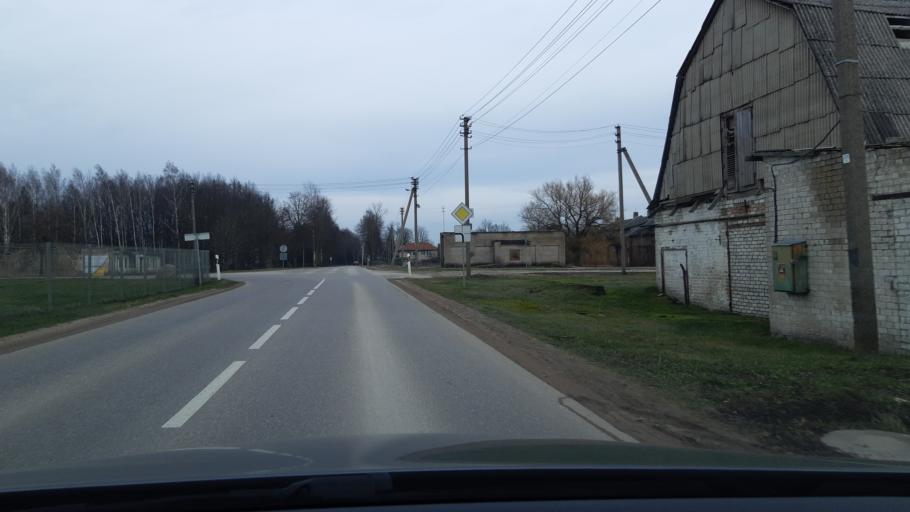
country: LT
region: Kauno apskritis
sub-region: Kaunas
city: Sargenai
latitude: 54.9555
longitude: 23.8606
